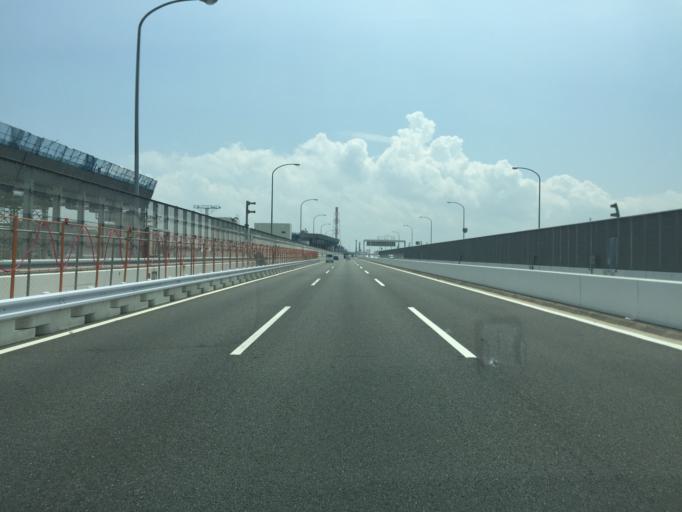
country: JP
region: Kanagawa
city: Yokohama
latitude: 35.4227
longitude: 139.6708
